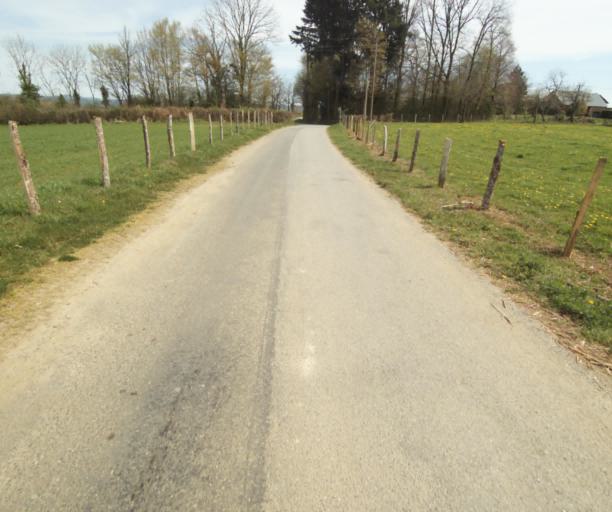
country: FR
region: Limousin
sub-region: Departement de la Correze
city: Naves
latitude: 45.3264
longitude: 1.7755
